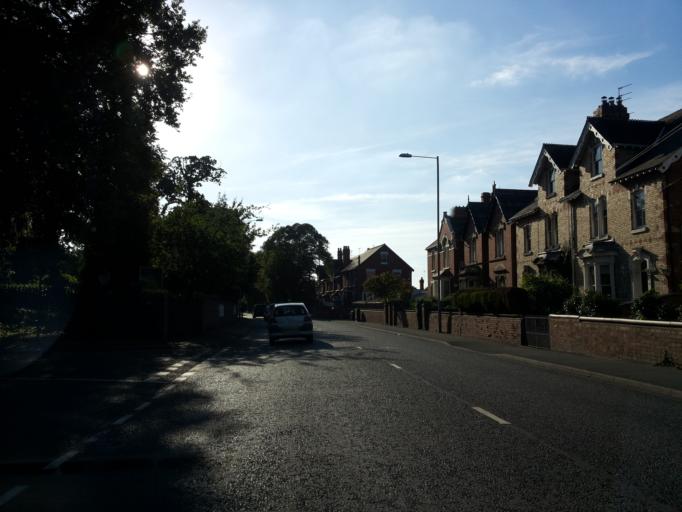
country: GB
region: England
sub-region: Worcestershire
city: Kidderminster
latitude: 52.3918
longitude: -2.2354
